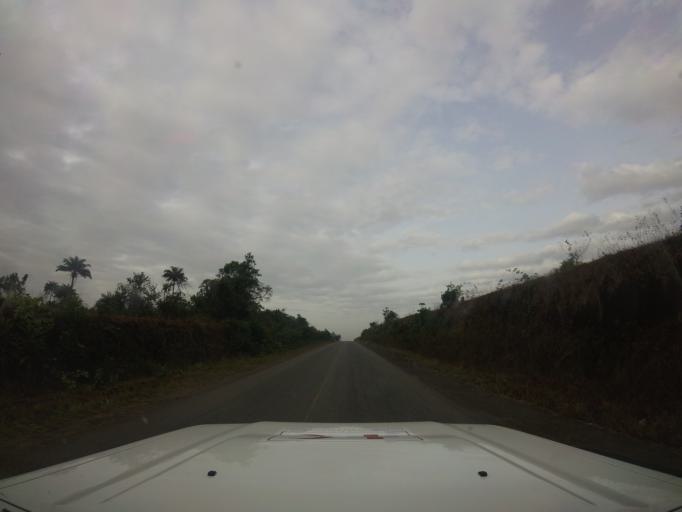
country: LR
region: Bomi
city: Tubmanburg
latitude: 6.7313
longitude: -11.0034
